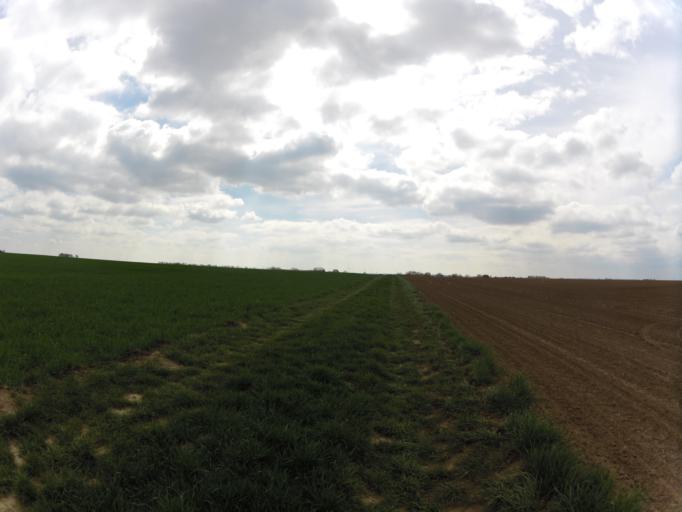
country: DE
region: Bavaria
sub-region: Regierungsbezirk Unterfranken
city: Giebelstadt
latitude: 49.6475
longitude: 9.9274
